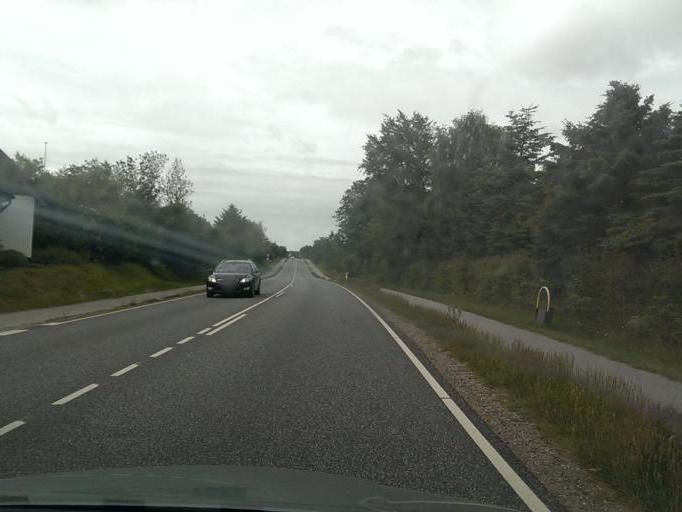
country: DK
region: North Denmark
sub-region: Hjorring Kommune
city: Hjorring
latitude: 57.4588
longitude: 9.9314
